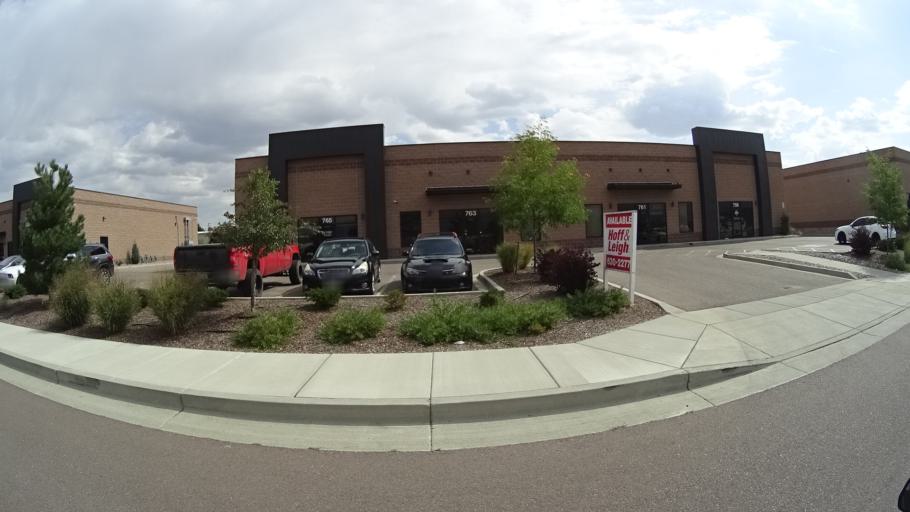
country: US
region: Colorado
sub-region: El Paso County
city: Cimarron Hills
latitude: 38.8433
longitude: -104.7320
